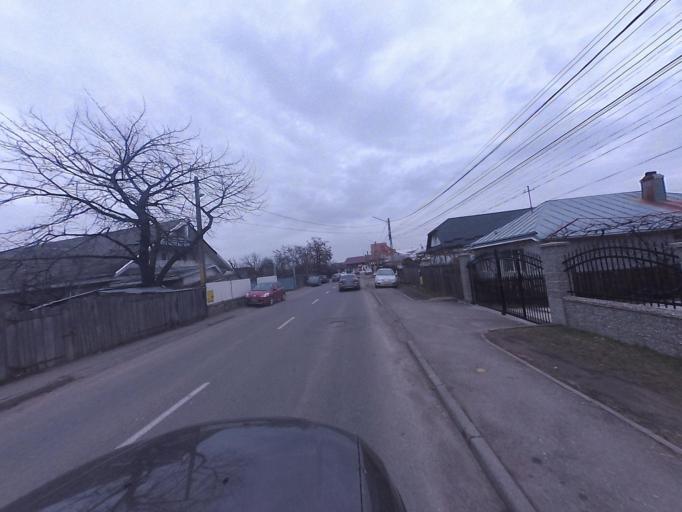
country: RO
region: Neamt
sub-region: Oras Targu Neamt
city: Targu Neamt
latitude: 47.2030
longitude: 26.3678
